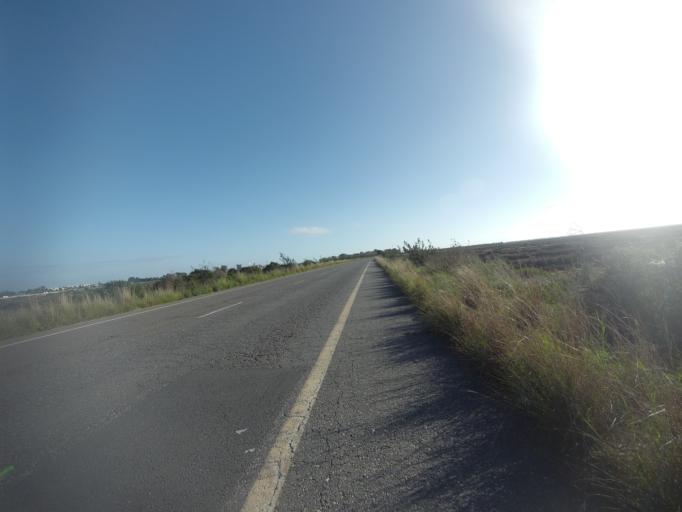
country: ES
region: Andalusia
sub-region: Provincia de Huelva
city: Huelva
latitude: 37.2451
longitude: -6.9665
